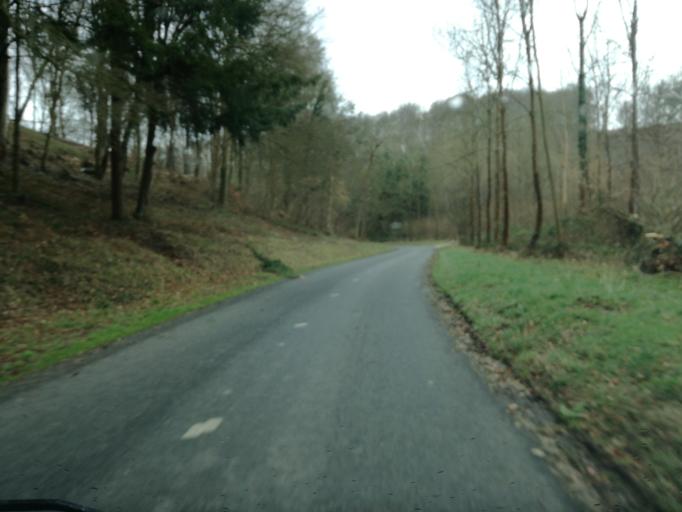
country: FR
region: Haute-Normandie
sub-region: Departement de la Seine-Maritime
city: Caudebec-en-Caux
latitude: 49.5597
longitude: 0.7411
